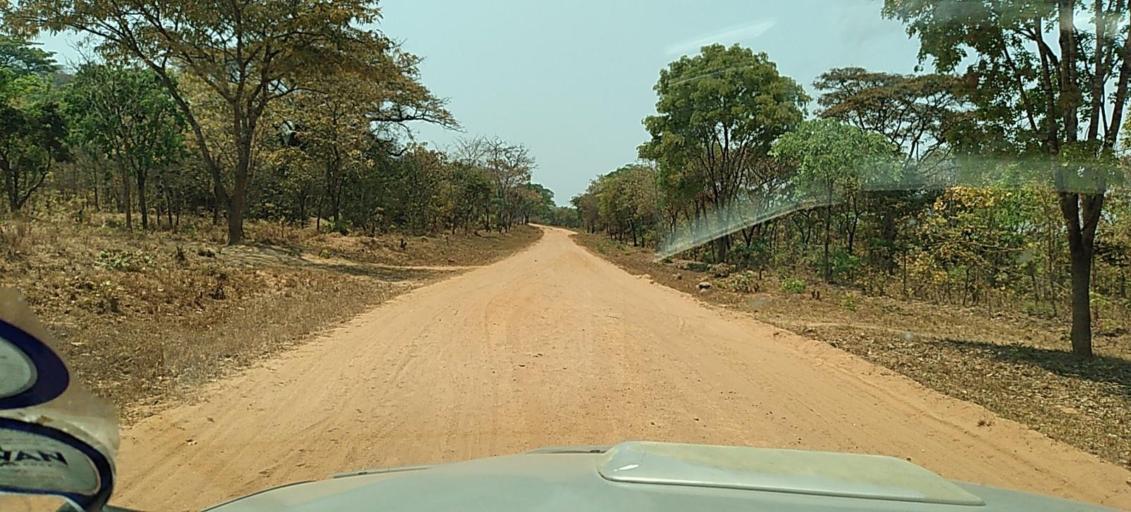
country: ZM
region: North-Western
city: Kasempa
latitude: -13.5508
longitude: 26.0236
